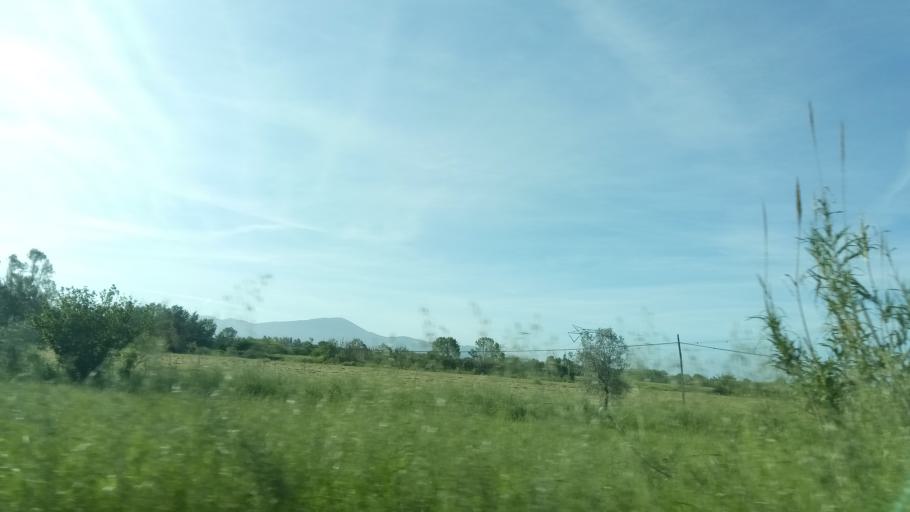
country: IT
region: Latium
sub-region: Provincia di Latina
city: Grunuovo-Campomaggiore San Luca
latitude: 41.2685
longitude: 13.7863
